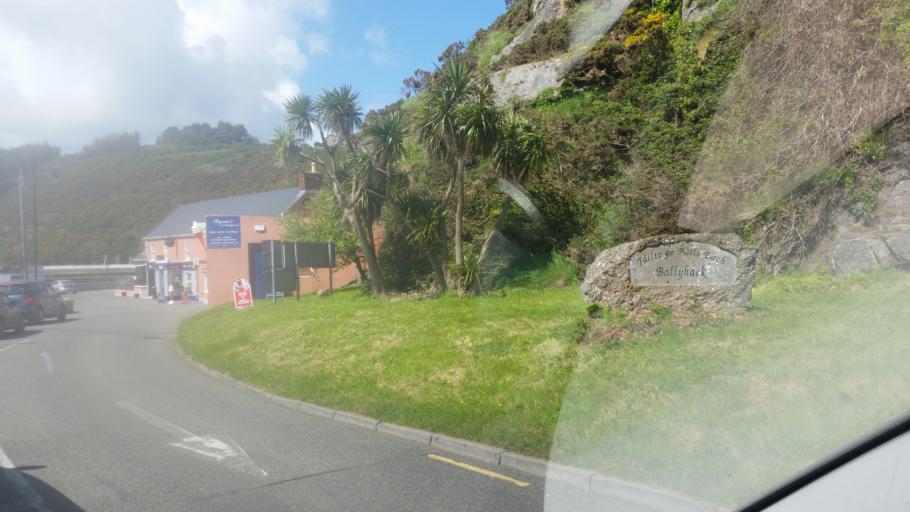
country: IE
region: Munster
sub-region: Waterford
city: Dunmore East
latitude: 52.2443
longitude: -6.9678
